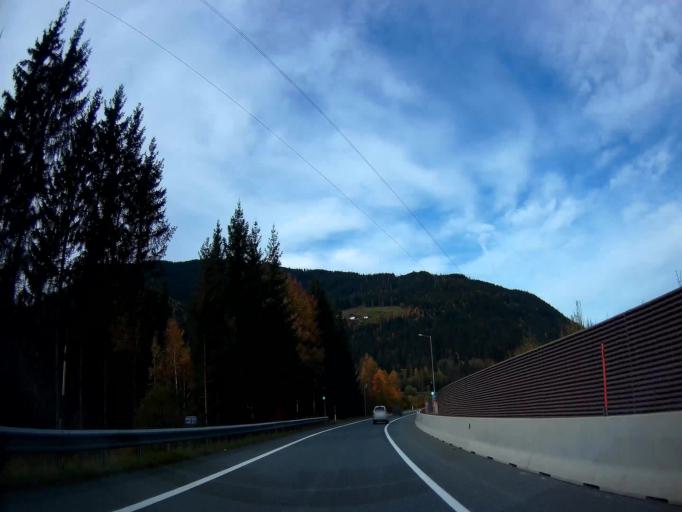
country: AT
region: Salzburg
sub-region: Politischer Bezirk Sankt Johann im Pongau
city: Eben im Pongau
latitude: 47.3932
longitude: 13.3990
